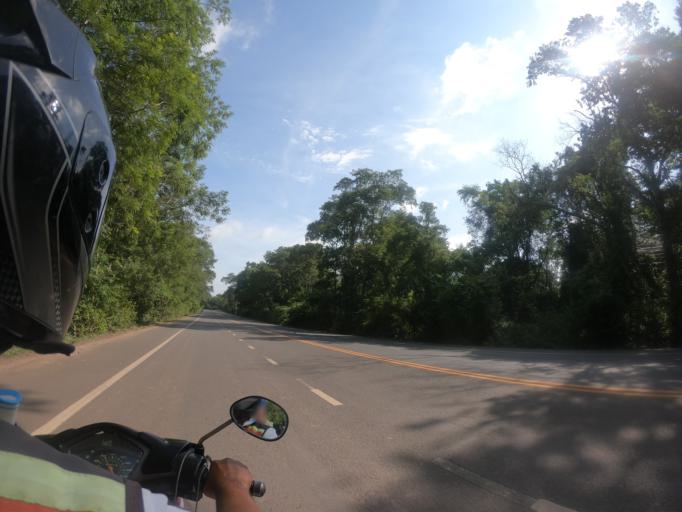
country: TH
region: Surin
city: Kap Choeng
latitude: 14.4452
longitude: 103.7007
